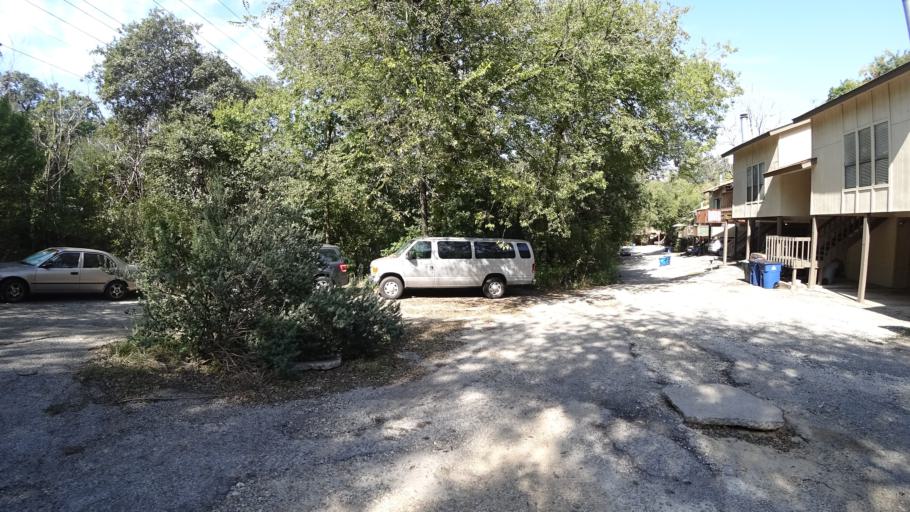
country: US
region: Texas
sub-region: Travis County
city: West Lake Hills
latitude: 30.3404
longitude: -97.7596
